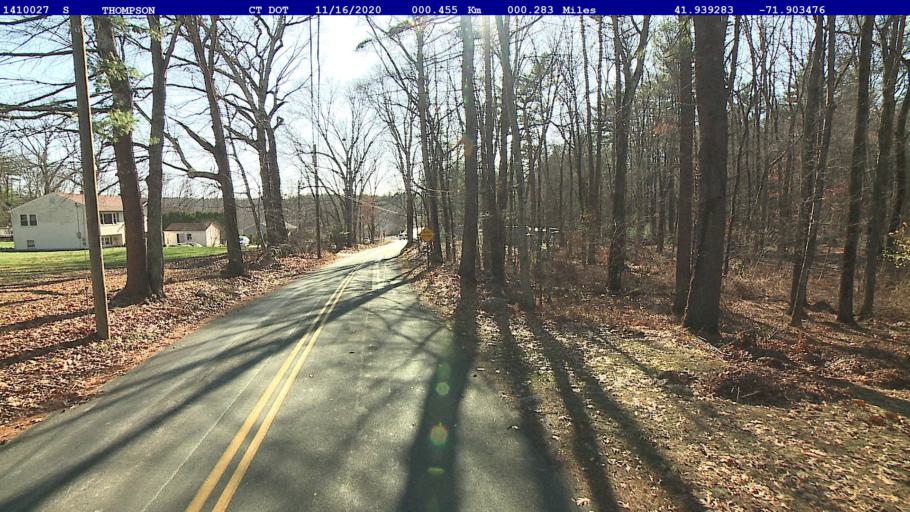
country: US
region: Connecticut
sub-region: Windham County
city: Putnam
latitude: 41.9393
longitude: -71.9035
